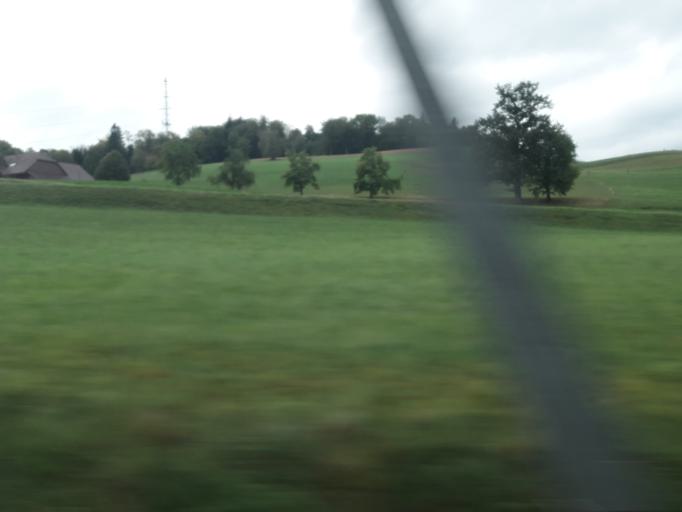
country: CH
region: Bern
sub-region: Thun District
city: Seftigen
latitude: 46.7877
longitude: 7.5464
